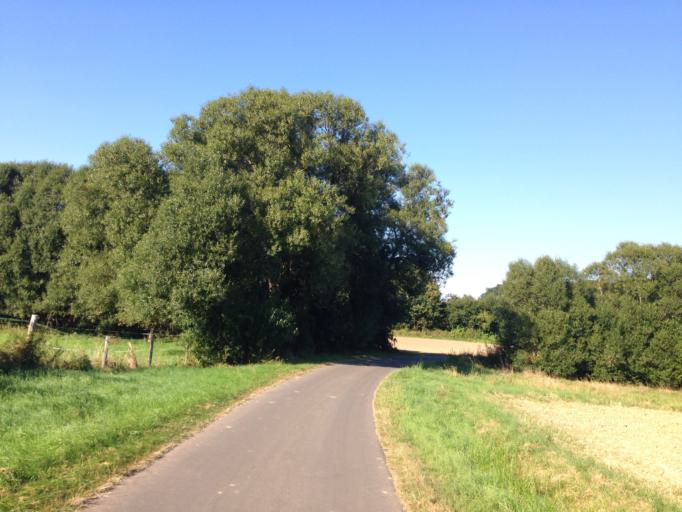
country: DE
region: Hesse
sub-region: Regierungsbezirk Giessen
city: Grunberg
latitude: 50.6195
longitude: 8.9438
